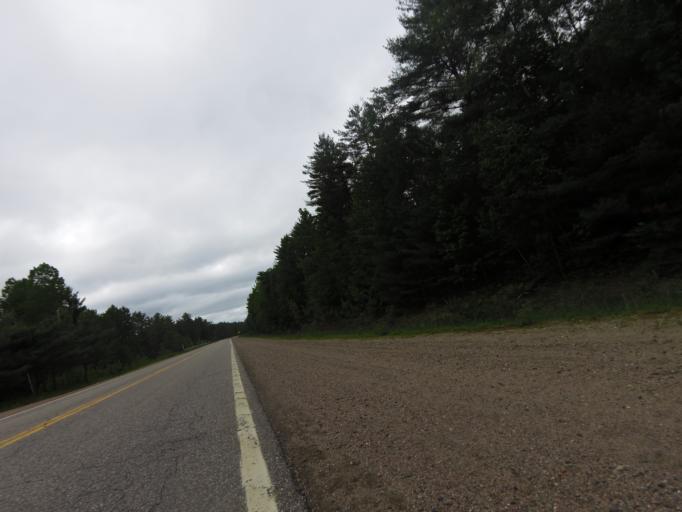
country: CA
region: Quebec
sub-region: Outaouais
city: Shawville
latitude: 45.8664
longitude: -76.4066
